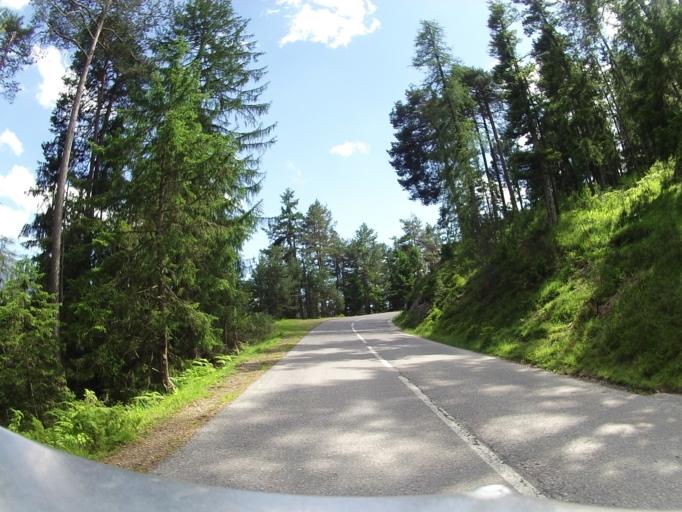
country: AT
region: Tyrol
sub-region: Politischer Bezirk Imst
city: Tarrenz
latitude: 47.2817
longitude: 10.7434
